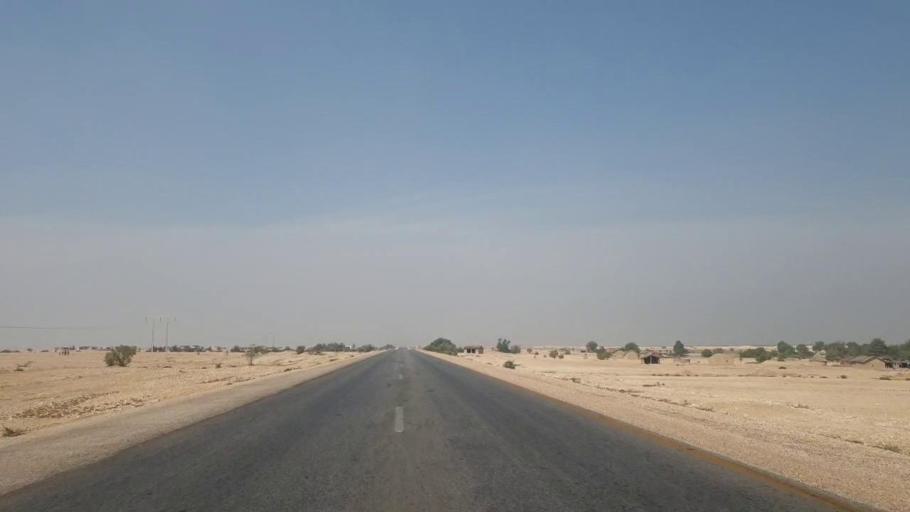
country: PK
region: Sindh
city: Hala
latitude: 25.8367
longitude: 68.2674
